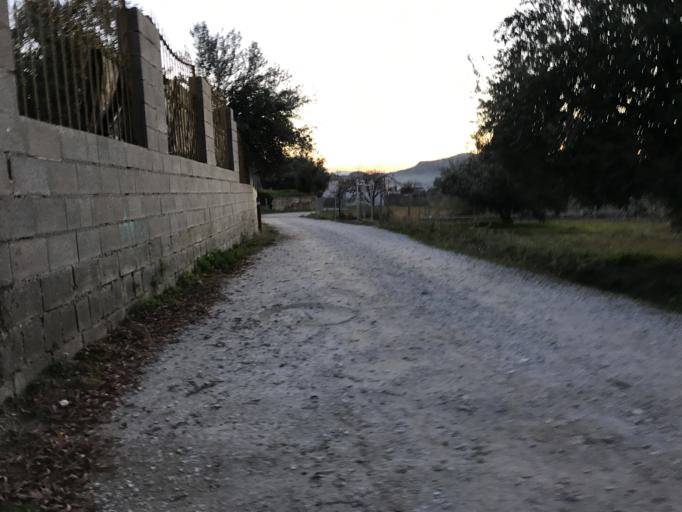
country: ES
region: Andalusia
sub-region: Provincia de Granada
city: Beas de Granada
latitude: 37.2243
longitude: -3.4780
